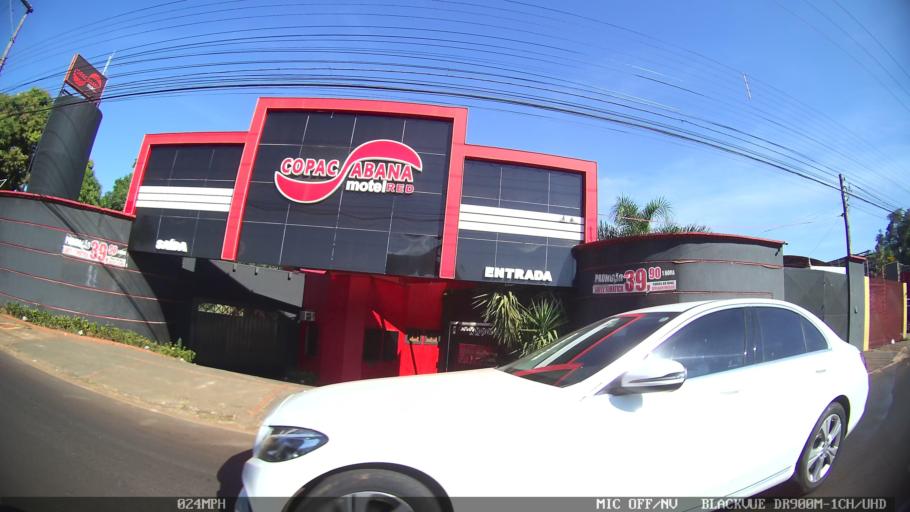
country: BR
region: Sao Paulo
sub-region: Ribeirao Preto
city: Ribeirao Preto
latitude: -21.1841
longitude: -47.7647
